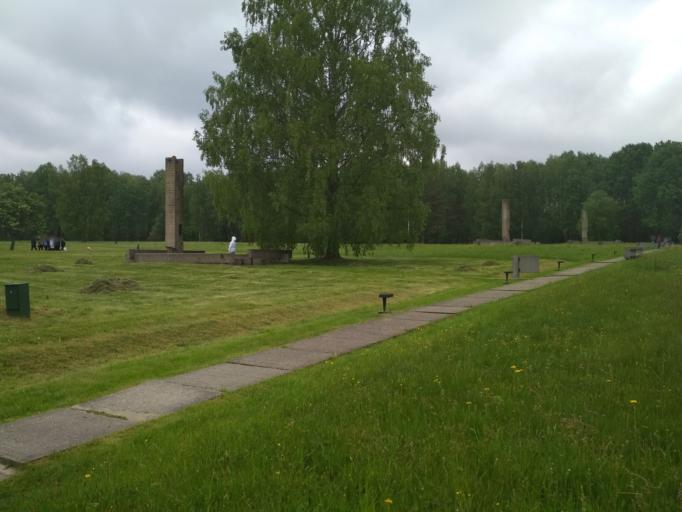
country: BY
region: Minsk
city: Plyeshchanitsy
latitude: 54.3352
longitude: 27.9442
